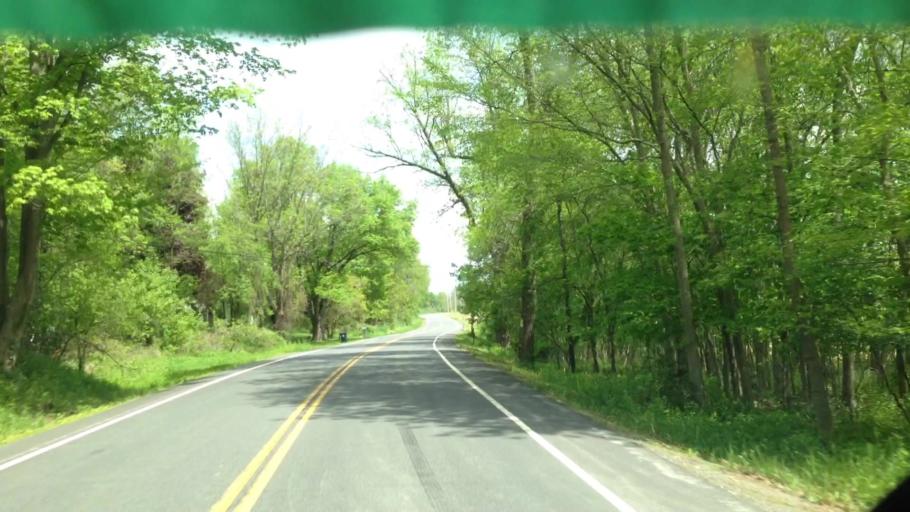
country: US
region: New York
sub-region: Dutchess County
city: Pine Plains
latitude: 42.0613
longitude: -73.6223
